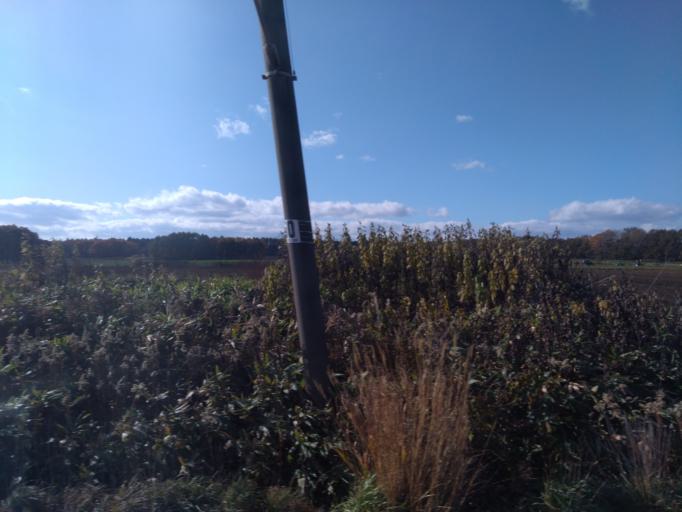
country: JP
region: Hokkaido
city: Kitahiroshima
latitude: 42.9520
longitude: 141.5706
